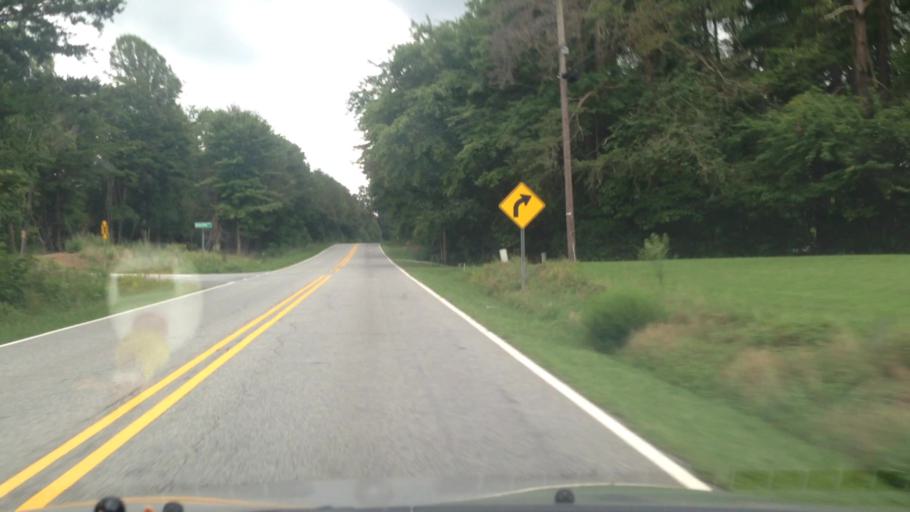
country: US
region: North Carolina
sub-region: Forsyth County
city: Walkertown
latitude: 36.2043
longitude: -80.1680
